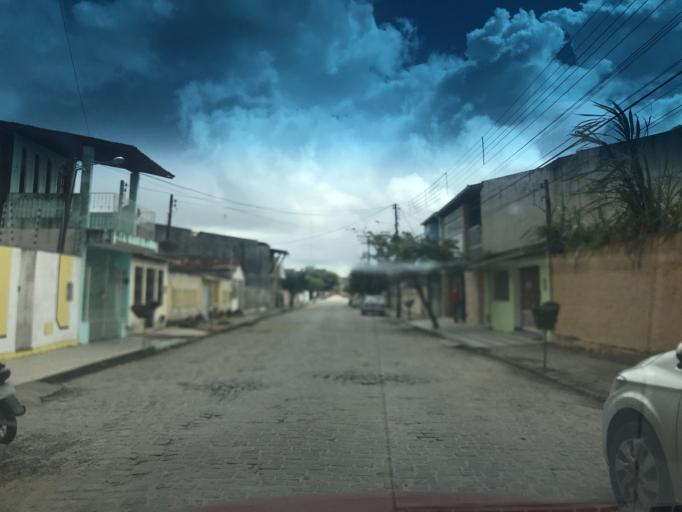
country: BR
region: Bahia
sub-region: Cruz Das Almas
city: Cruz das Almas
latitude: -12.6762
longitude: -39.0988
